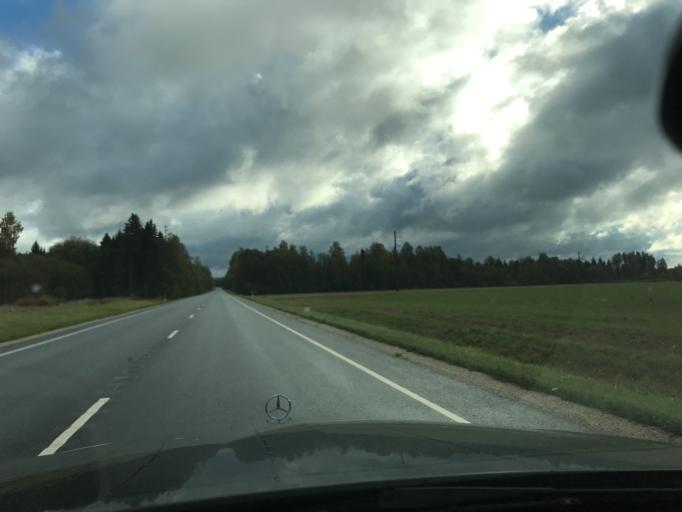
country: EE
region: Viljandimaa
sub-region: Karksi vald
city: Karksi-Nuia
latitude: 58.0105
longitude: 25.7293
